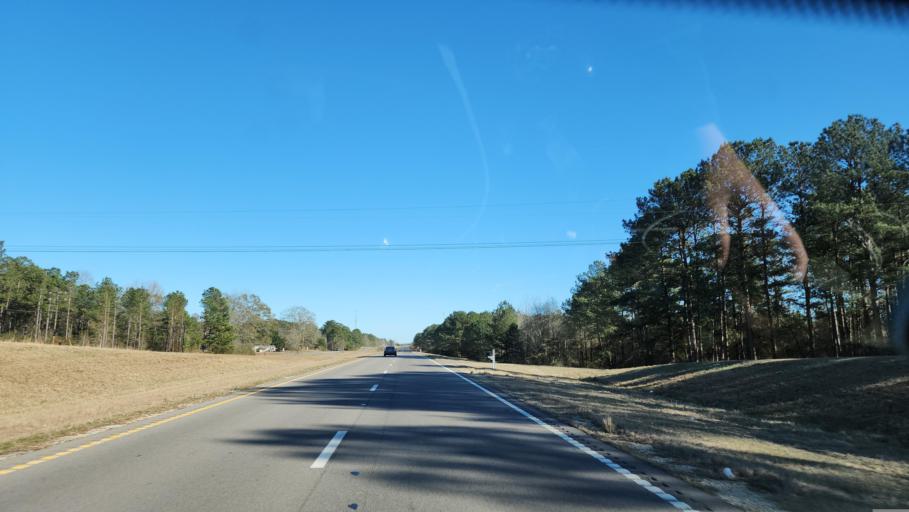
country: US
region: Mississippi
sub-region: Jones County
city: Sharon
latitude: 31.7063
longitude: -88.9381
